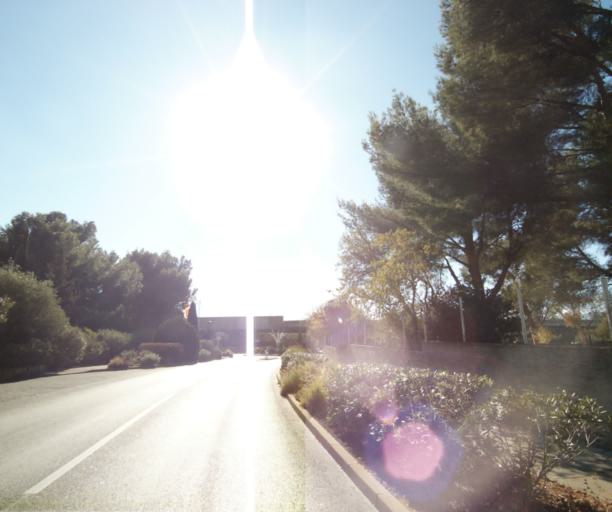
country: FR
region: Provence-Alpes-Cote d'Azur
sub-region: Departement des Bouches-du-Rhone
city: Ceyreste
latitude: 43.2100
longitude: 5.6288
